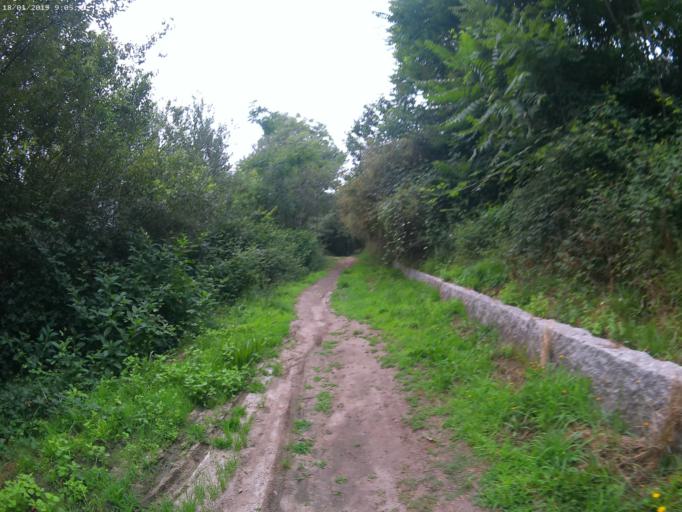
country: PT
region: Viana do Castelo
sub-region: Ponte da Barca
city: Ponte da Barca
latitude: 41.8063
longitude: -8.4454
